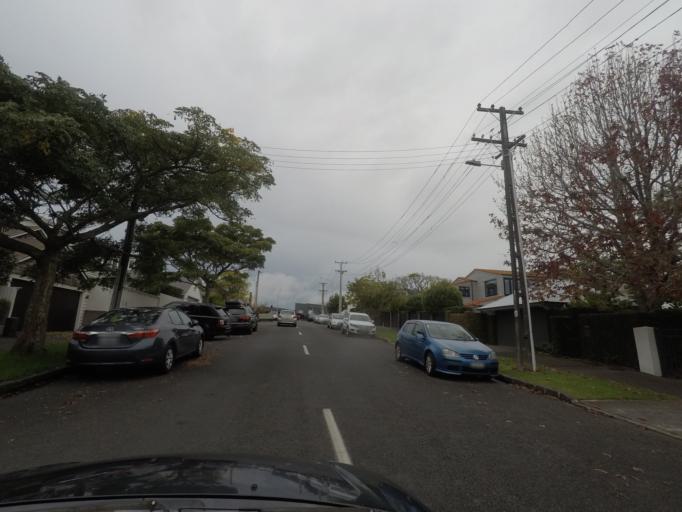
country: NZ
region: Auckland
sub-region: Auckland
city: Auckland
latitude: -36.8447
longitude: 174.7337
